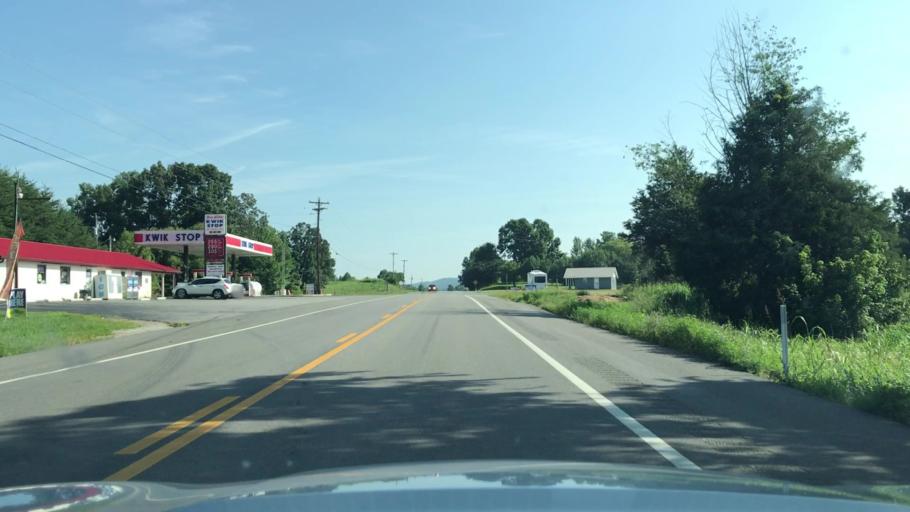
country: US
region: Tennessee
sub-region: Pickett County
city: Byrdstown
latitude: 36.5148
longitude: -85.1703
